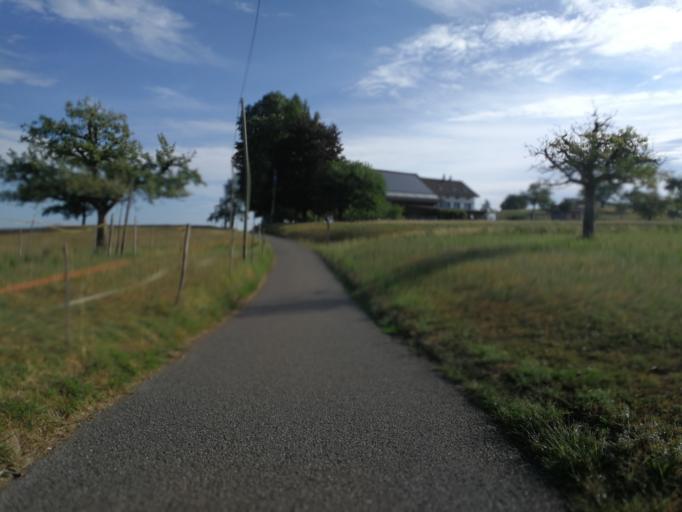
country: CH
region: Zurich
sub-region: Bezirk Meilen
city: Oetwil am See
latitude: 47.2668
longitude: 8.7408
